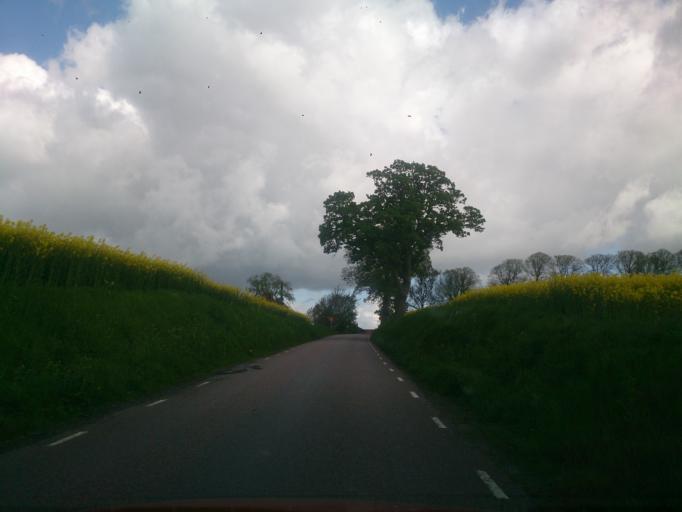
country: SE
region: Skane
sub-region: Ystads Kommun
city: Ystad
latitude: 55.4604
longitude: 13.7066
